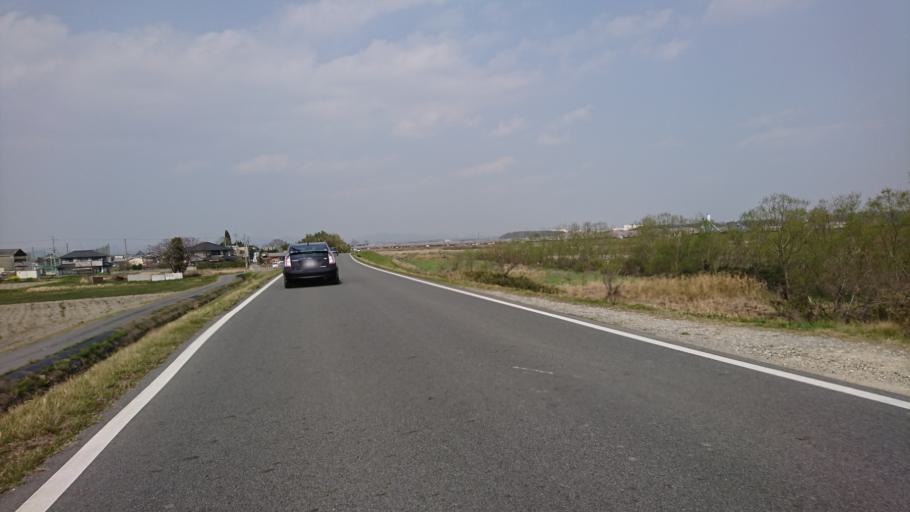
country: JP
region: Hyogo
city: Ono
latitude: 34.8675
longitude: 134.9188
